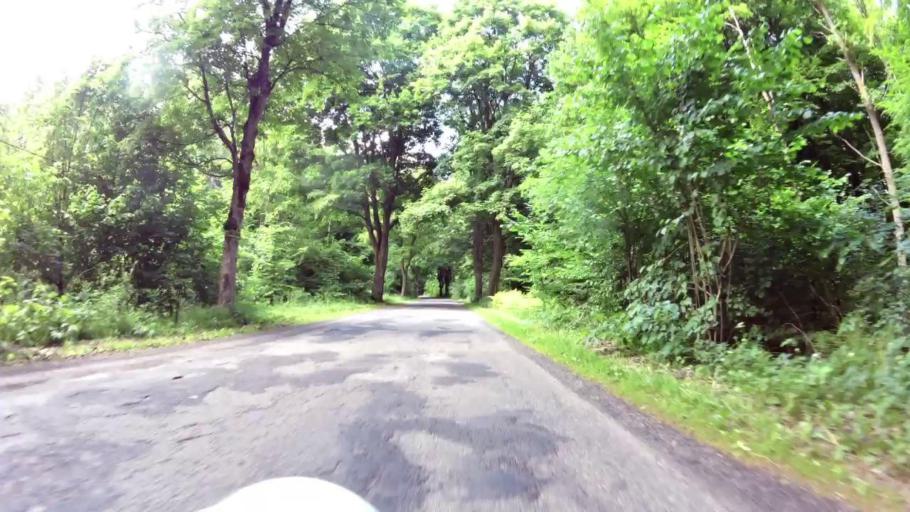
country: PL
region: West Pomeranian Voivodeship
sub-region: Powiat koszalinski
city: Bobolice
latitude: 53.9645
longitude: 16.7085
